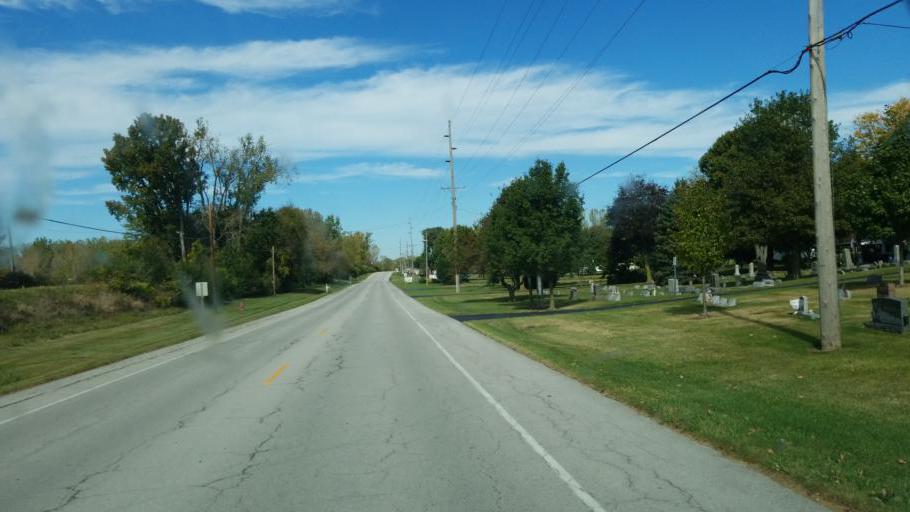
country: US
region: Ohio
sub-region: Erie County
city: Huron
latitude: 41.3752
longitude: -82.5457
